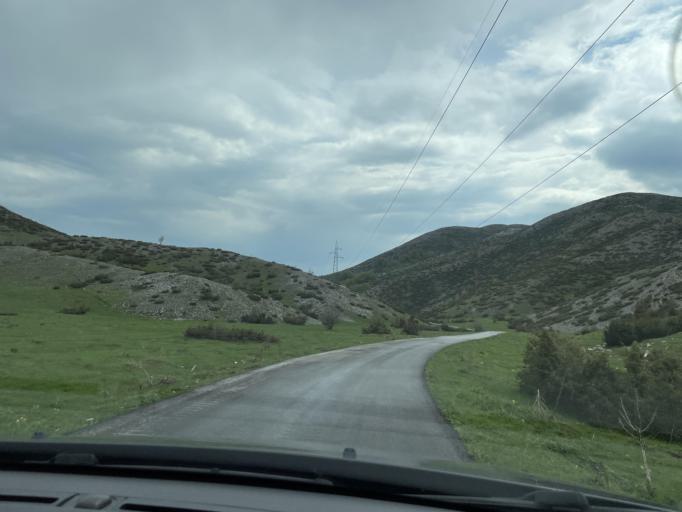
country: MK
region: Opstina Rostusa
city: Rostusha
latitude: 41.6156
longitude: 20.6827
